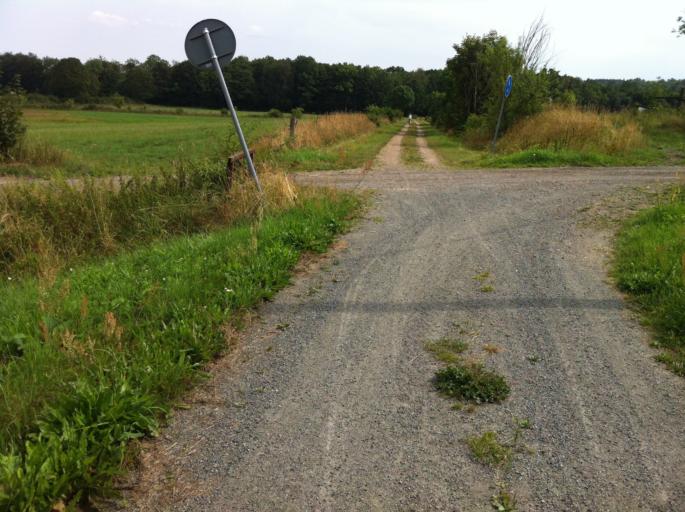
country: SE
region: Skane
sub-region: Kristianstads Kommun
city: Onnestad
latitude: 55.9448
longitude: 13.9023
